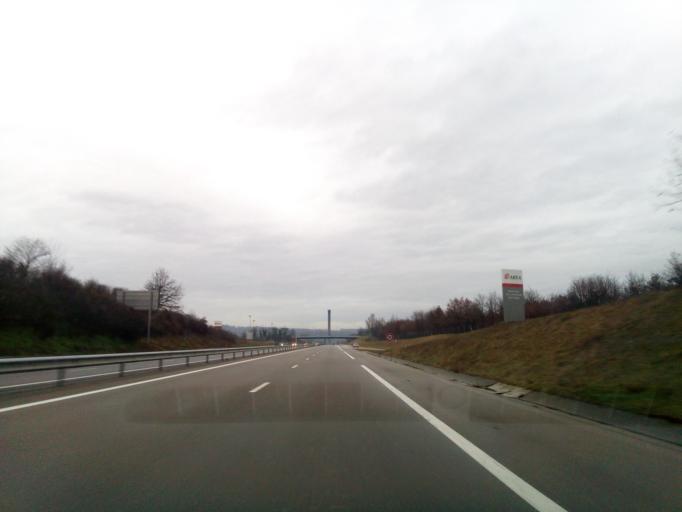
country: FR
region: Rhone-Alpes
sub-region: Departement de l'Isere
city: Saint-Lattier
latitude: 45.0753
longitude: 5.2120
